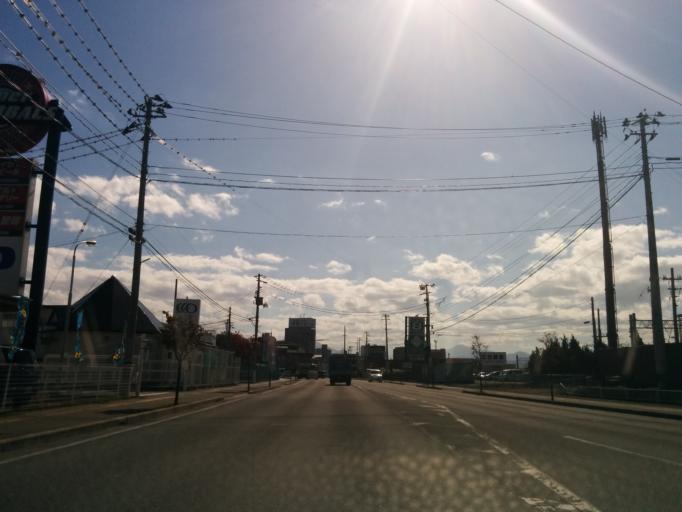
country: JP
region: Fukushima
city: Kitakata
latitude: 37.5130
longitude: 139.9316
